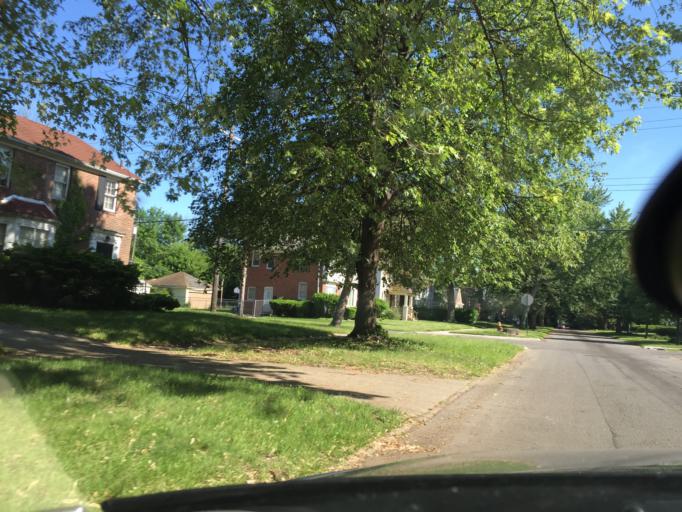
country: US
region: Michigan
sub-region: Oakland County
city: Southfield
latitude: 42.4102
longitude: -83.2276
